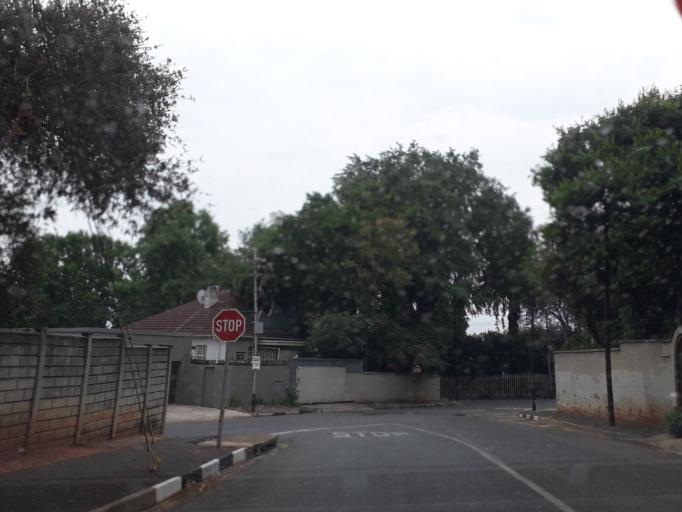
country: ZA
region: Gauteng
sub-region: City of Johannesburg Metropolitan Municipality
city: Johannesburg
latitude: -26.1658
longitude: 28.0780
